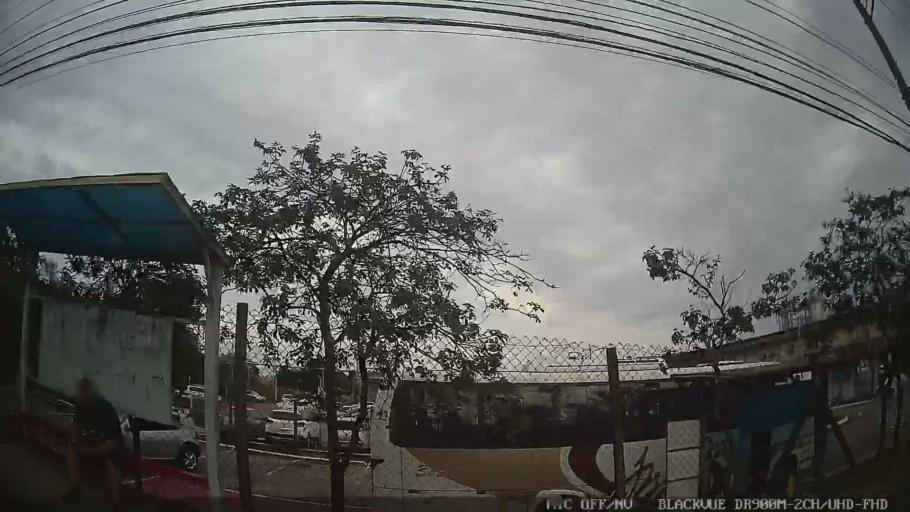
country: BR
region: Sao Paulo
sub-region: Maua
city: Maua
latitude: -23.6421
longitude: -46.4669
